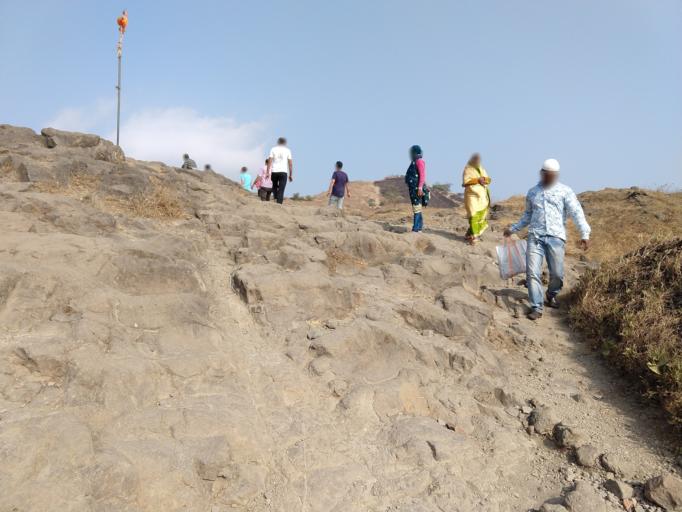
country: IN
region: Maharashtra
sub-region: Pune Division
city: Lonavla
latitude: 18.7079
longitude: 73.4770
